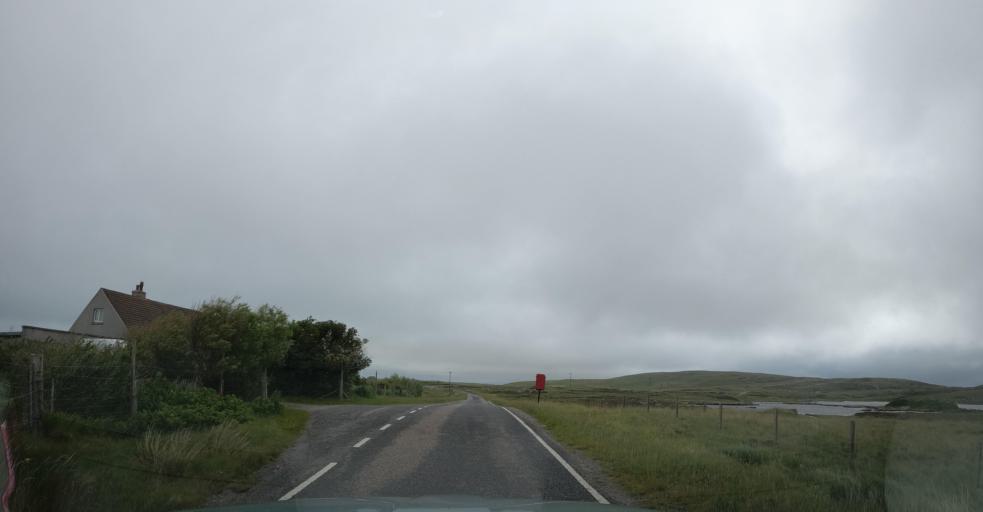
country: GB
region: Scotland
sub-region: Eilean Siar
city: Isle of North Uist
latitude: 57.6805
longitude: -7.2126
